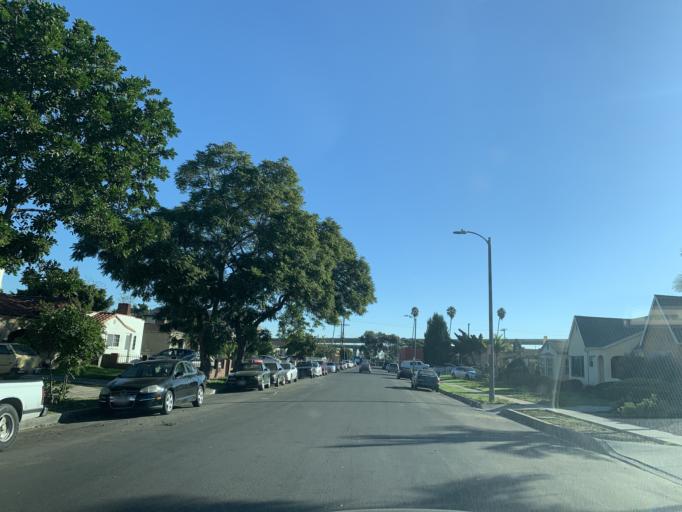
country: US
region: California
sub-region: Los Angeles County
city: Westmont
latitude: 33.9319
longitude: -118.2846
